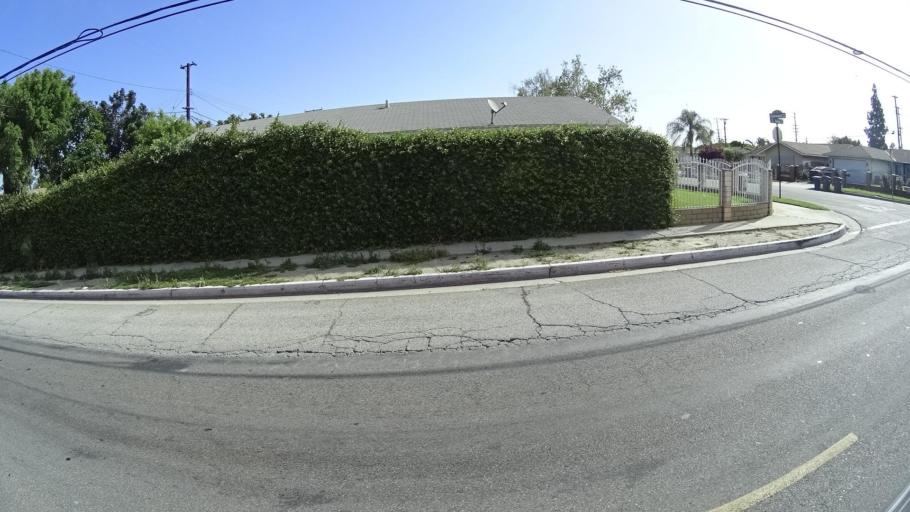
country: US
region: California
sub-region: Los Angeles County
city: West Puente Valley
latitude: 34.0377
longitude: -117.9732
